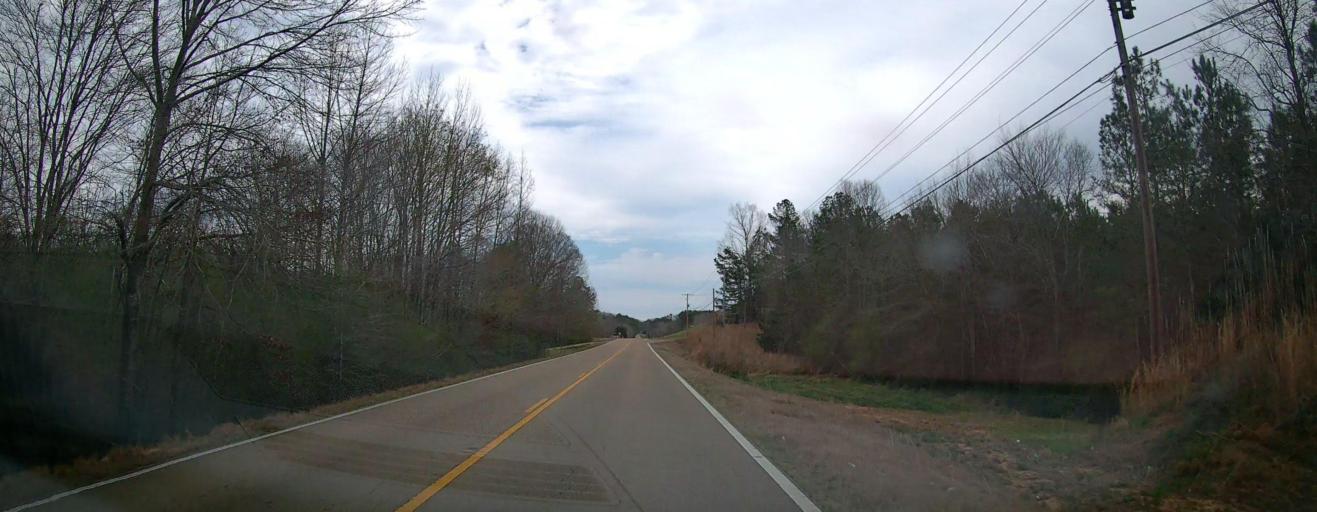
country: US
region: Mississippi
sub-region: Itawamba County
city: Fulton
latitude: 34.2553
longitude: -88.3118
